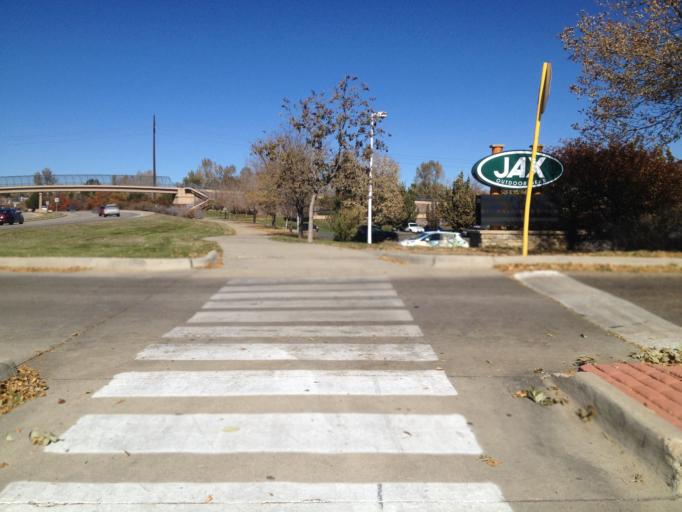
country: US
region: Colorado
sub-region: Boulder County
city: Lafayette
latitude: 39.9888
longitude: -105.0982
